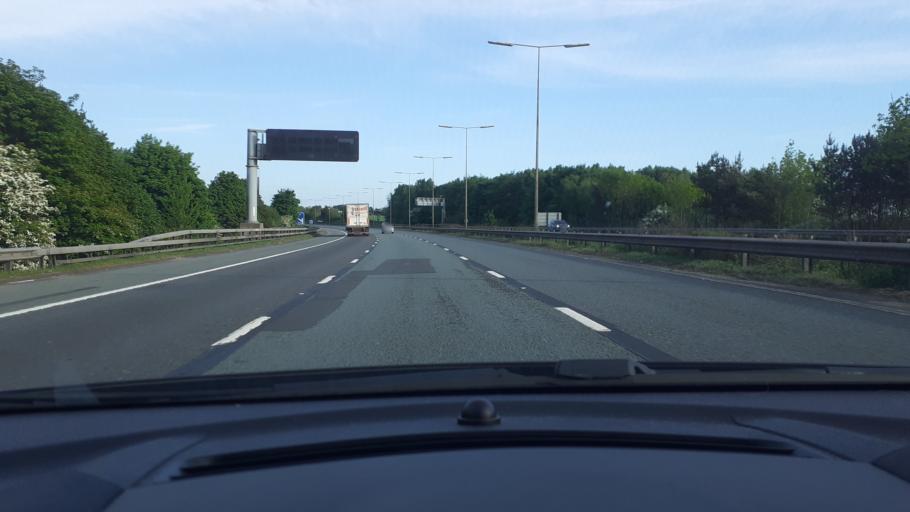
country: GB
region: England
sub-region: St. Helens
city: Newton-le-Willows
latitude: 53.4528
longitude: -2.6007
